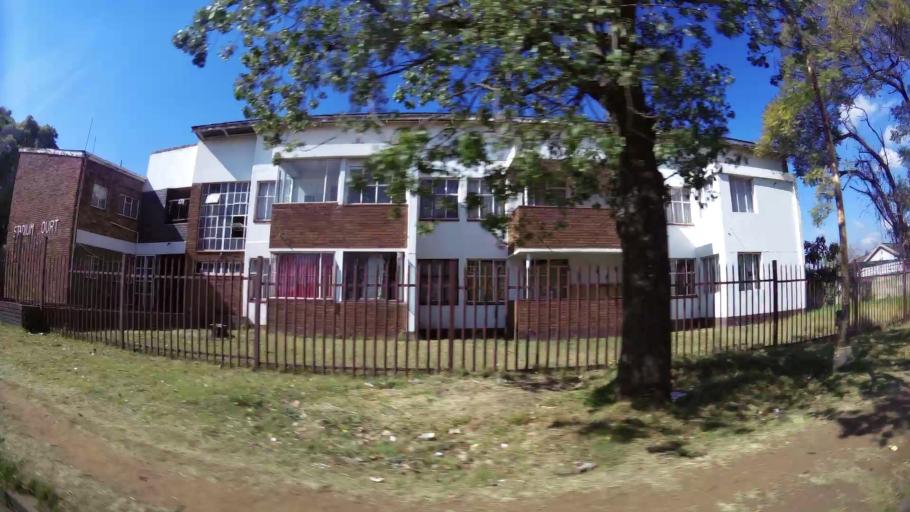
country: ZA
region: Mpumalanga
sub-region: Nkangala District Municipality
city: Witbank
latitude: -25.8818
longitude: 29.2194
